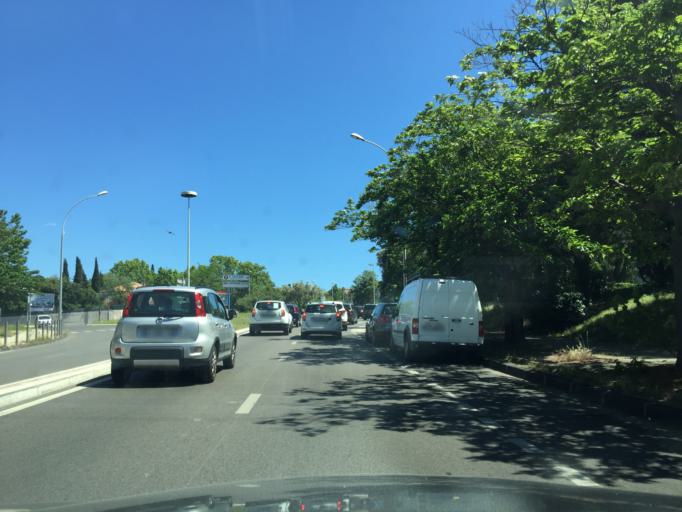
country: FR
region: Provence-Alpes-Cote d'Azur
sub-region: Departement des Bouches-du-Rhone
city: Marseille 09
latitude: 43.2466
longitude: 5.3940
